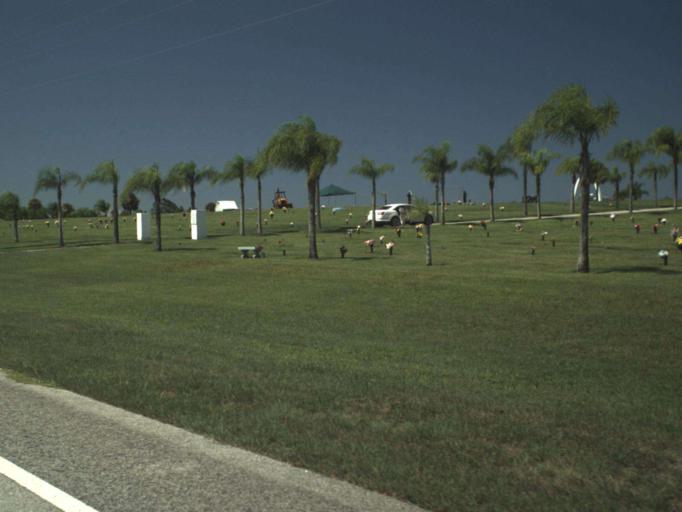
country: US
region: Florida
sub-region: Saint Lucie County
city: Lakewood Park
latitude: 27.5440
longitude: -80.3667
